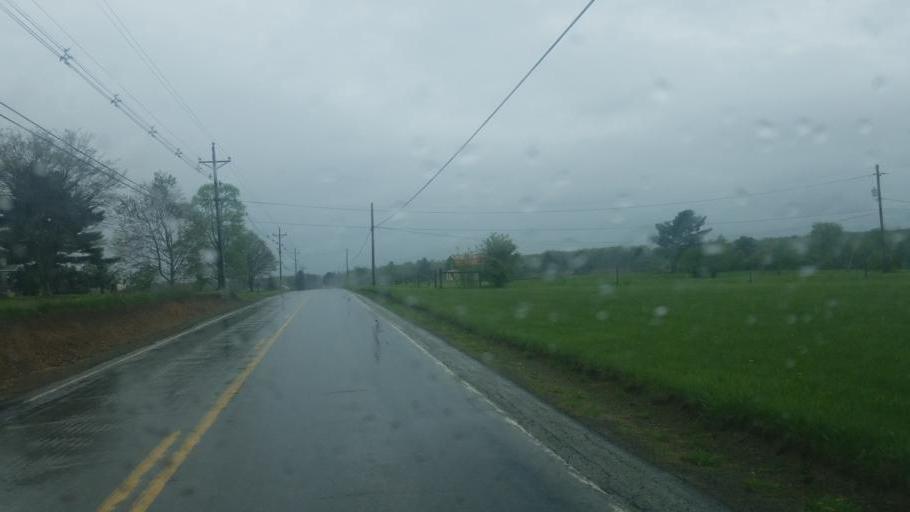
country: US
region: Pennsylvania
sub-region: Forest County
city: Tionesta
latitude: 41.3952
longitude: -79.3446
